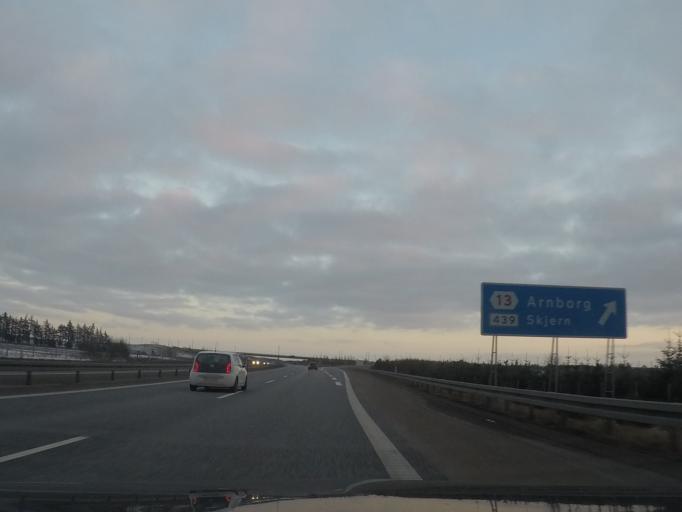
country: DK
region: Central Jutland
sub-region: Herning Kommune
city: Lind
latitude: 56.0182
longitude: 9.0193
